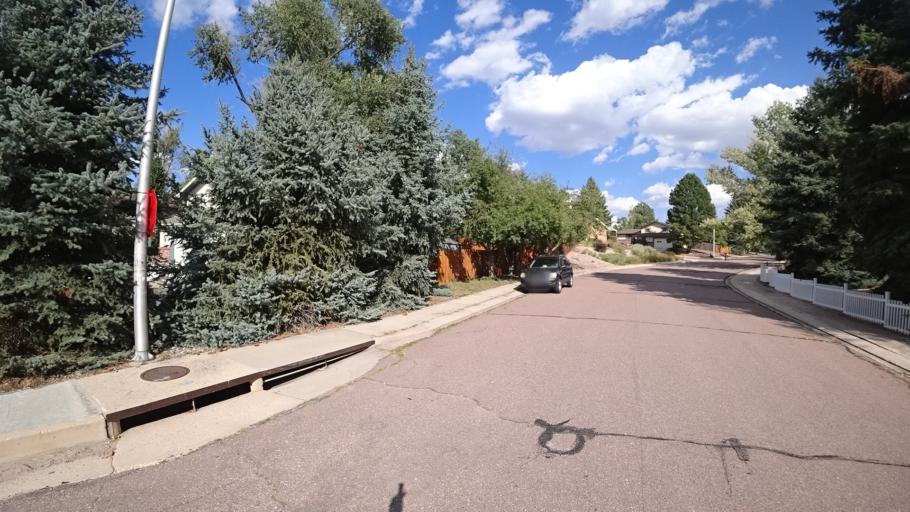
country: US
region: Colorado
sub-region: El Paso County
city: Cimarron Hills
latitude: 38.8737
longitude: -104.7381
